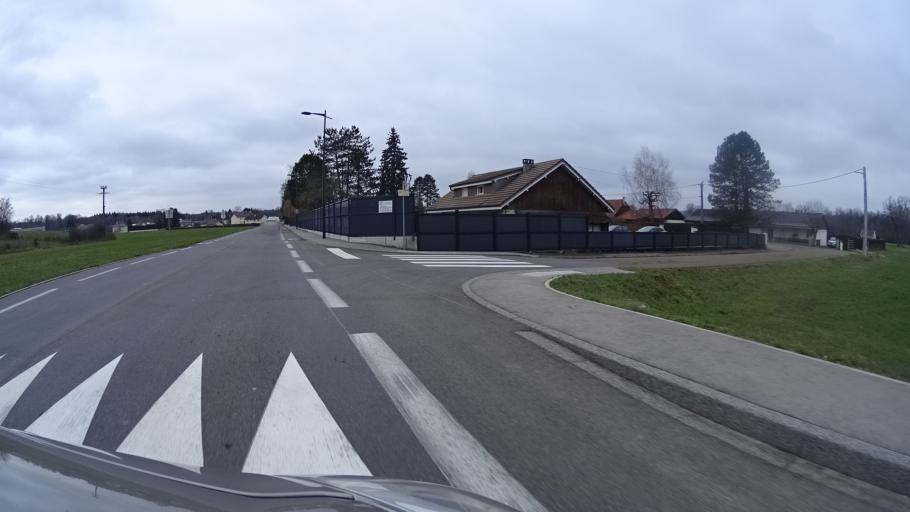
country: FR
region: Franche-Comte
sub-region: Departement du Doubs
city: Saone
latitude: 47.2124
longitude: 6.1057
